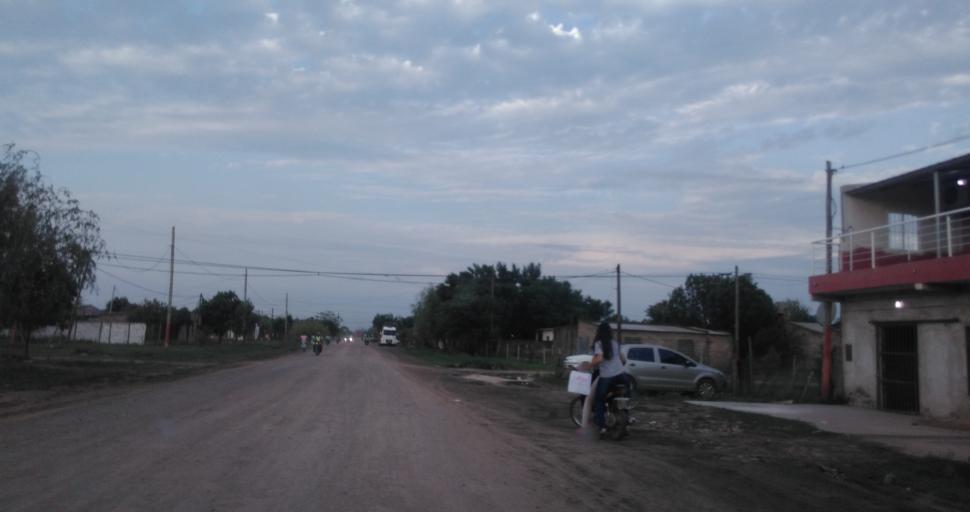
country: AR
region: Chaco
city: Resistencia
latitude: -27.4826
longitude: -59.0020
